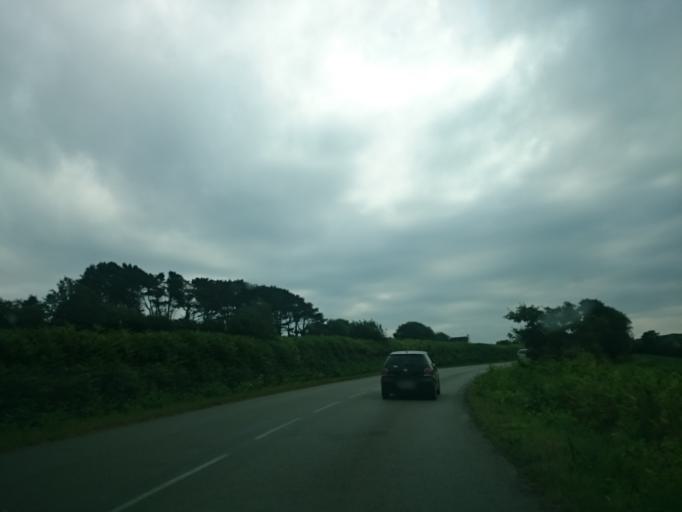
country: FR
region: Brittany
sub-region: Departement du Finistere
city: Saint-Renan
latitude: 48.4126
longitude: -4.6547
